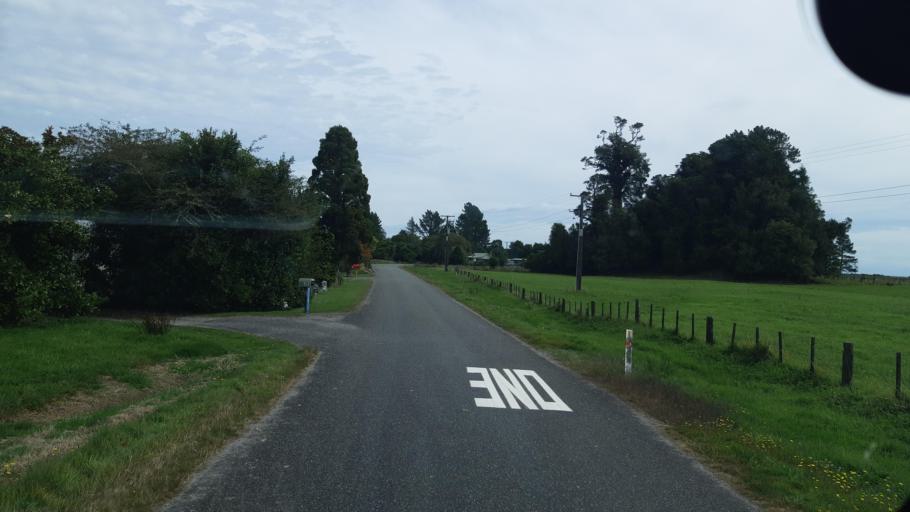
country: NZ
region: West Coast
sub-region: Westland District
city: Hokitika
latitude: -42.9749
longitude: 170.6845
